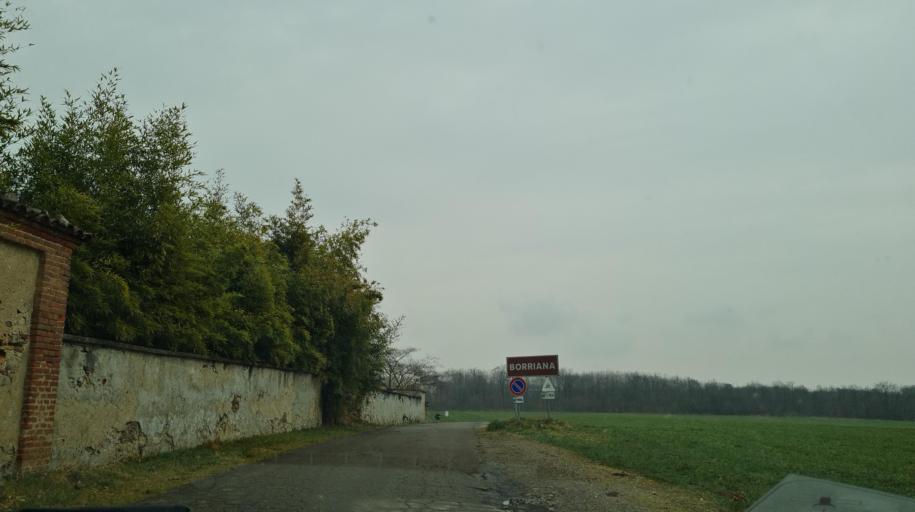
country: IT
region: Piedmont
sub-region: Provincia di Biella
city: Borriana
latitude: 45.5111
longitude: 8.0275
